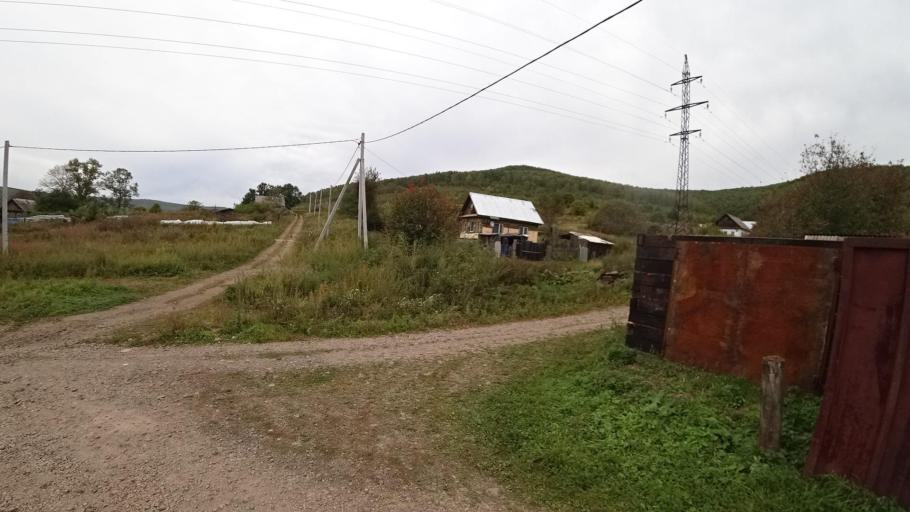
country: RU
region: Jewish Autonomous Oblast
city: Khingansk
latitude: 49.0379
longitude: 131.0606
